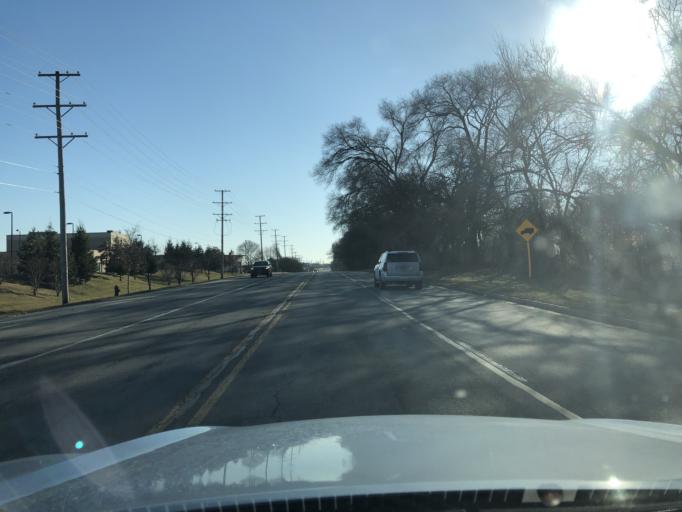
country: US
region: Illinois
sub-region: DuPage County
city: Itasca
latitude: 41.9767
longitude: -87.9982
